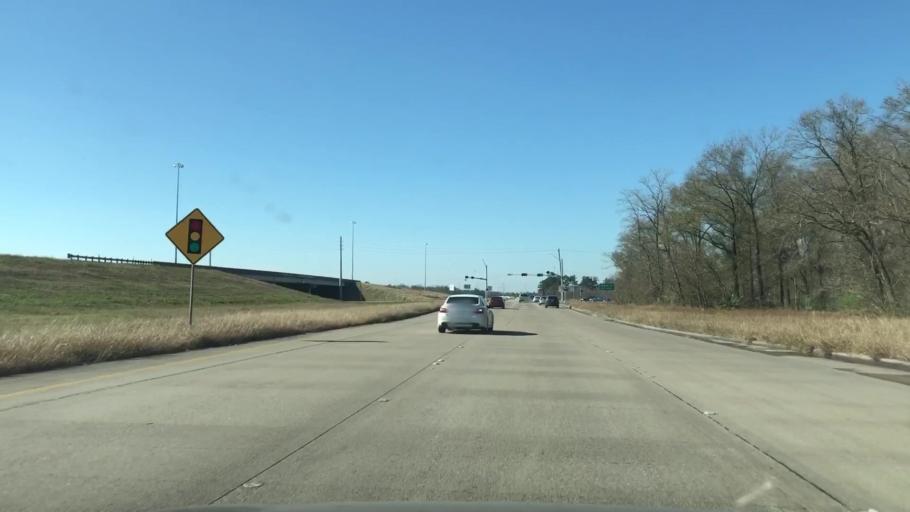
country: US
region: Texas
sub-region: Harris County
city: Cloverleaf
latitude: 29.8314
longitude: -95.1808
